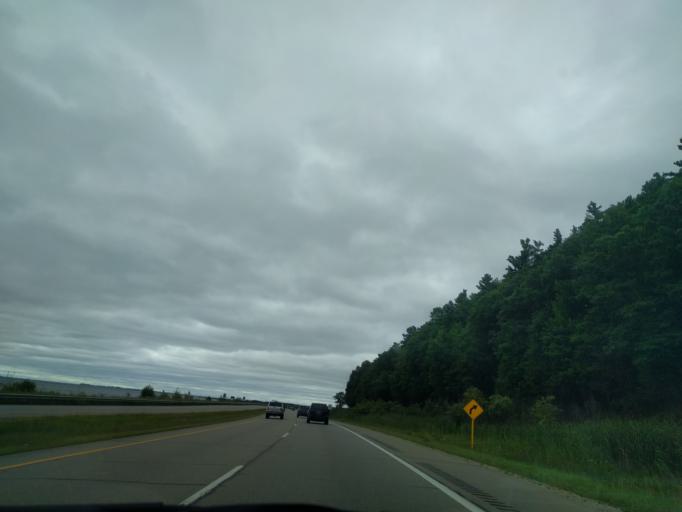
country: US
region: Michigan
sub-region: Delta County
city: Gladstone
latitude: 45.8317
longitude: -87.0431
